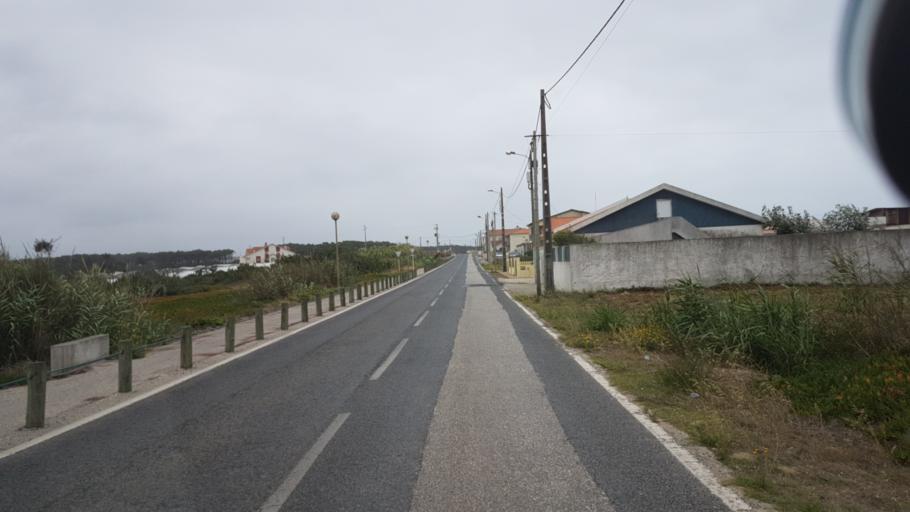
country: PT
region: Lisbon
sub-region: Torres Vedras
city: Silveira
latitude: 39.1636
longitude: -9.3600
